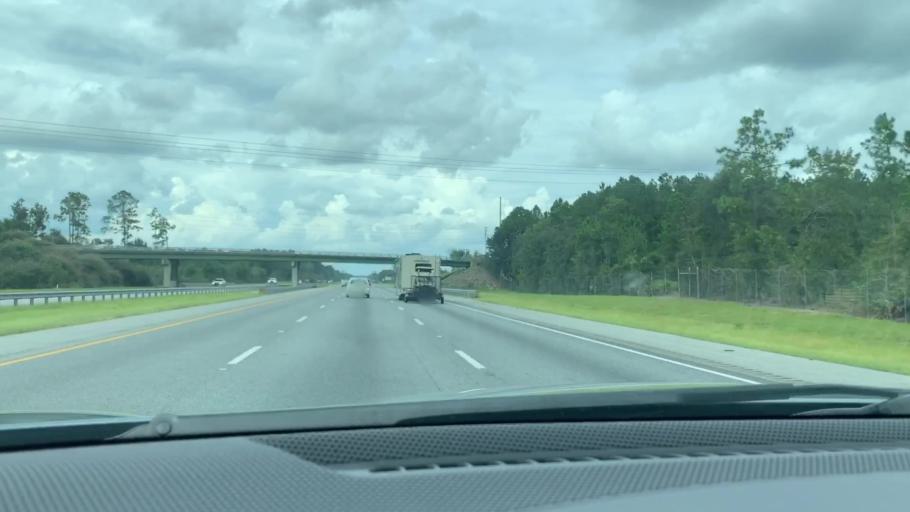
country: US
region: Georgia
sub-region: McIntosh County
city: Darien
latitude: 31.4302
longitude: -81.4435
